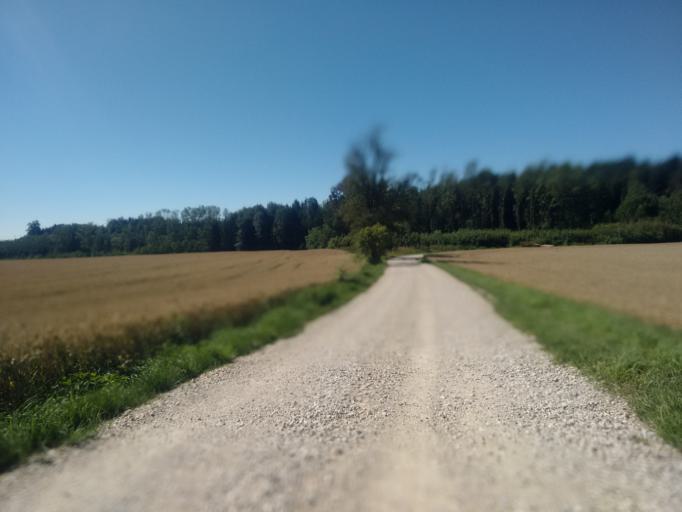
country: AT
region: Upper Austria
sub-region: Wels-Land
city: Buchkirchen
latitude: 48.2198
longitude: 14.0076
